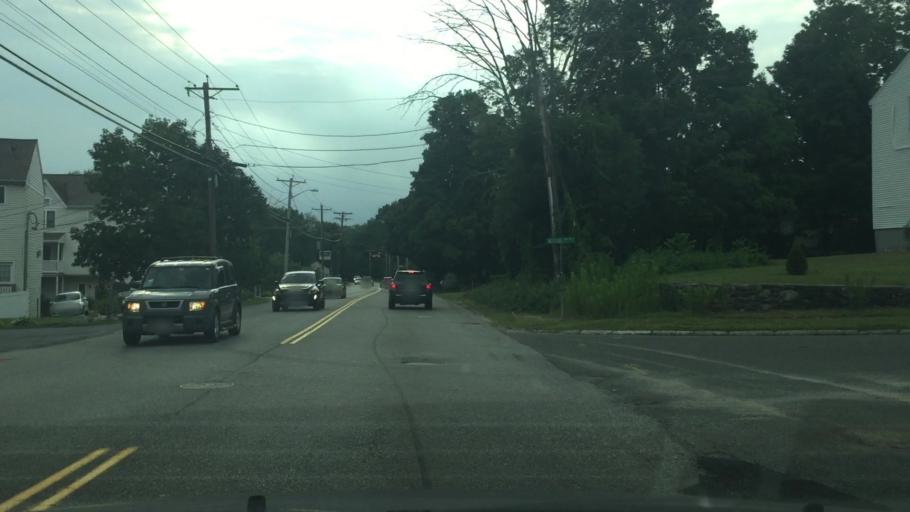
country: US
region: New Hampshire
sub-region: Rockingham County
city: Atkinson
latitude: 42.7881
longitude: -71.1368
